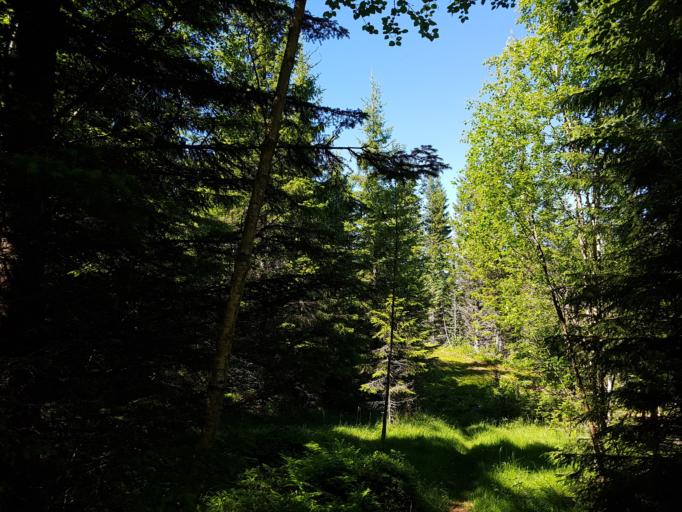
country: NO
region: Sor-Trondelag
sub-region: Melhus
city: Melhus
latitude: 63.4392
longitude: 10.2088
